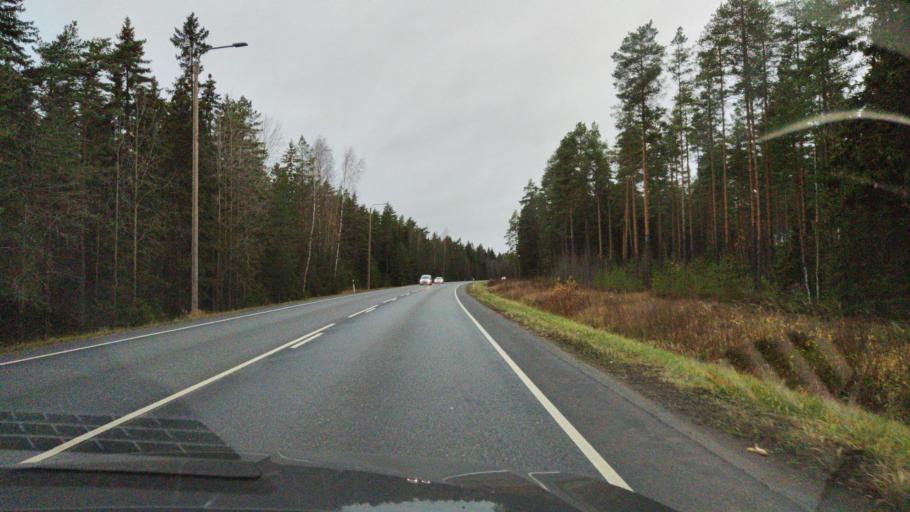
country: FI
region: Satakunta
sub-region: Rauma
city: Koeylioe
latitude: 61.0910
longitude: 22.2452
